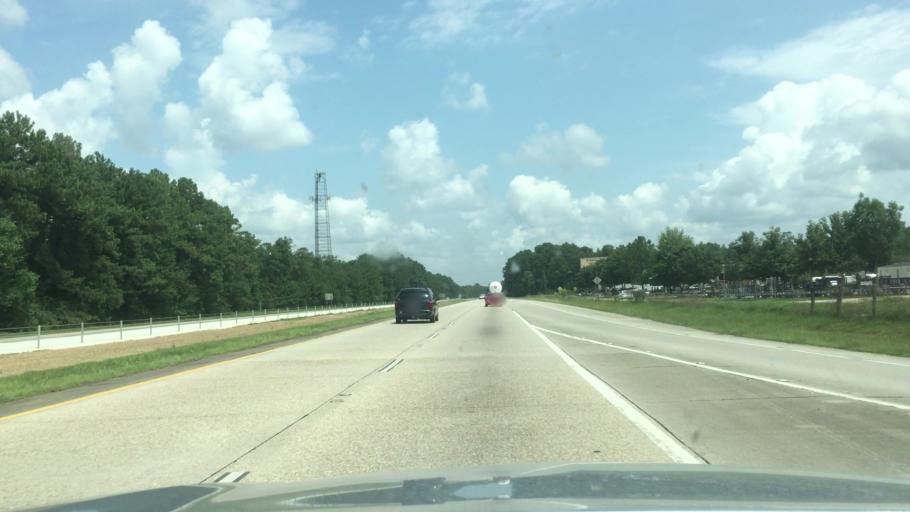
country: US
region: Louisiana
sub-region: Saint Tammany Parish
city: Pearl River
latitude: 30.3547
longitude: -89.7407
